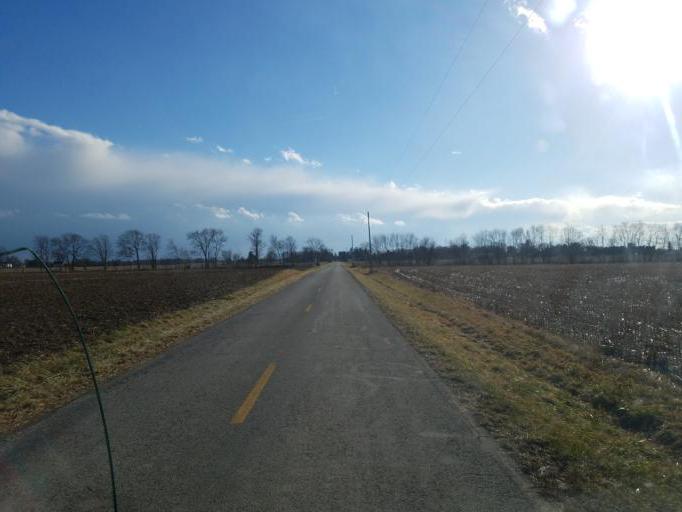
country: US
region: Ohio
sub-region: Marion County
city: Prospect
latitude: 40.3919
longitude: -83.1452
